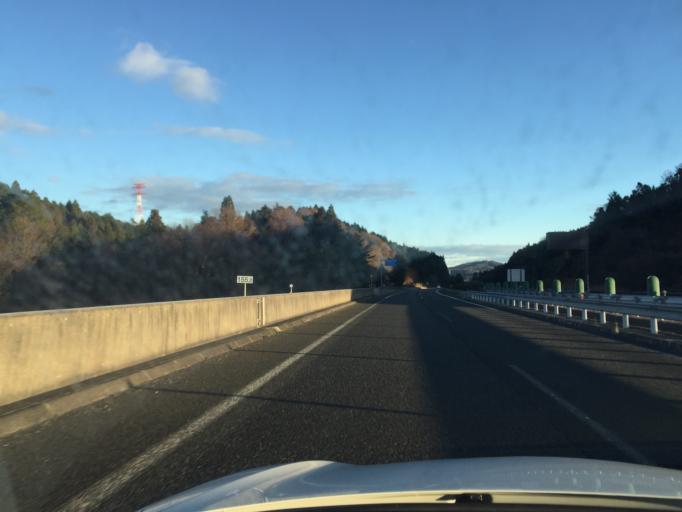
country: JP
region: Ibaraki
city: Kitaibaraki
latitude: 36.9071
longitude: 140.7521
